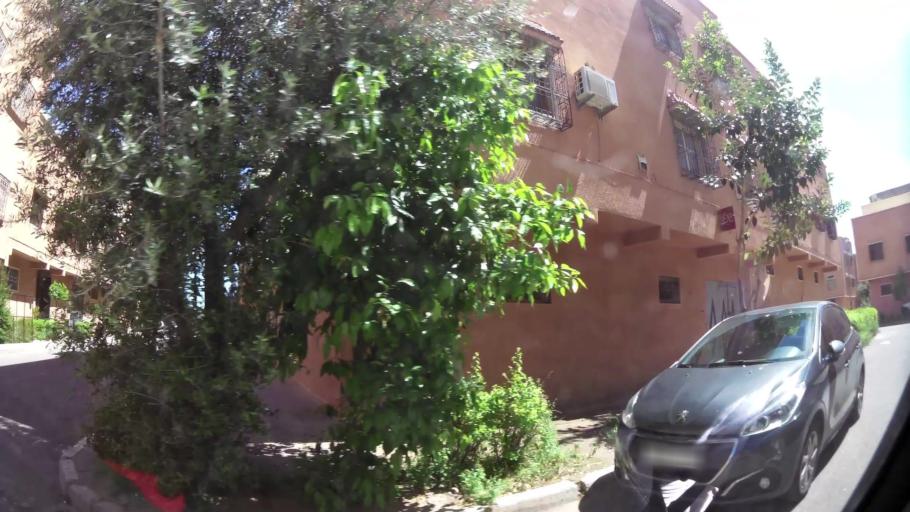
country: MA
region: Marrakech-Tensift-Al Haouz
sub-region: Marrakech
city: Marrakesh
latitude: 31.6589
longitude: -7.9869
